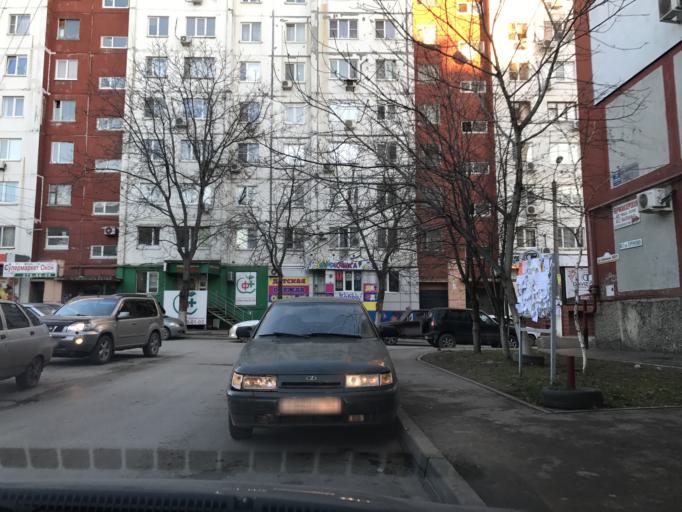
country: RU
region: Rostov
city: Rostov-na-Donu
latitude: 47.2314
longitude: 39.6190
